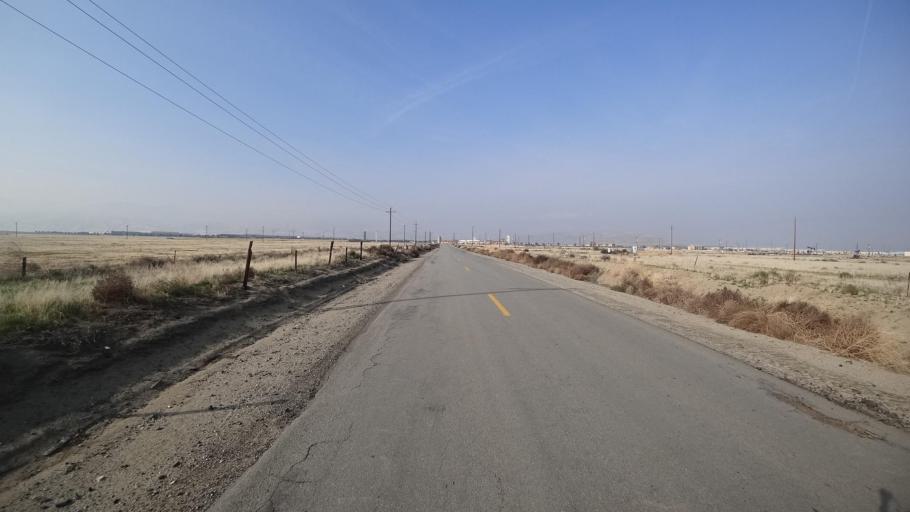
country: US
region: California
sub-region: Kern County
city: Lebec
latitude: 34.9845
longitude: -118.9318
